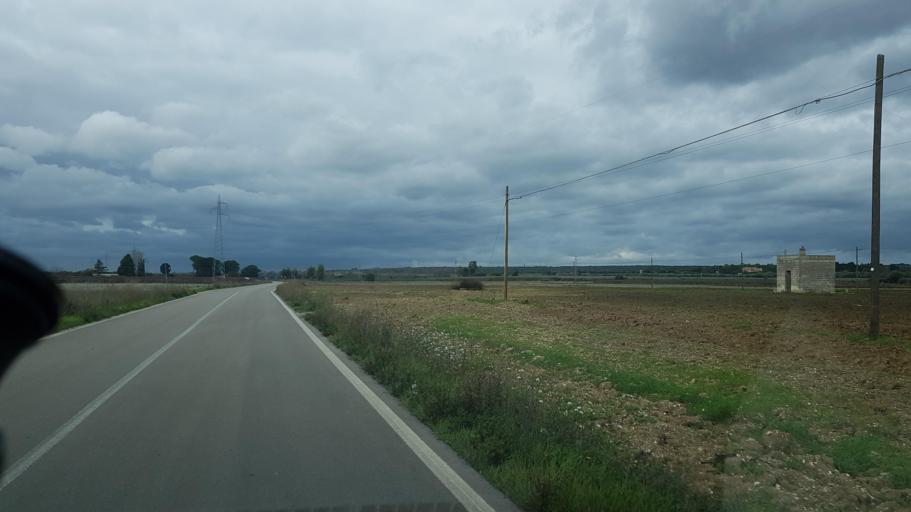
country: IT
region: Apulia
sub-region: Provincia di Brindisi
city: Francavilla Fontana
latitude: 40.5425
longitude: 17.5614
